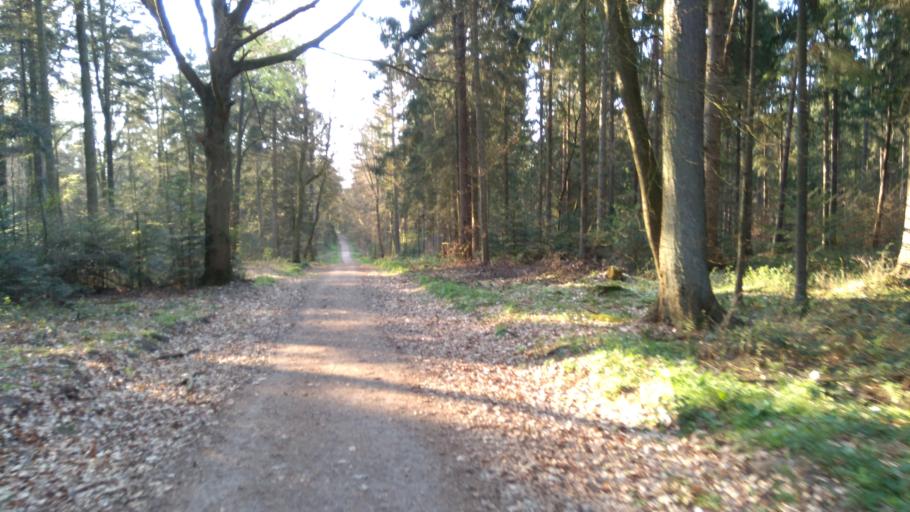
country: DE
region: Lower Saxony
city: Buxtehude
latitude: 53.4703
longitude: 9.6502
